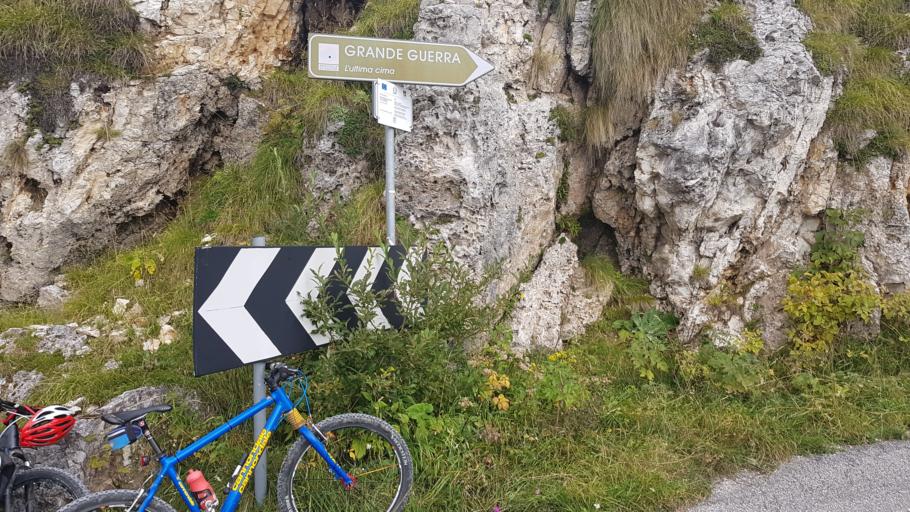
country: IT
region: Veneto
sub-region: Provincia di Treviso
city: Crespano del Grappa
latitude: 45.8595
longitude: 11.8022
